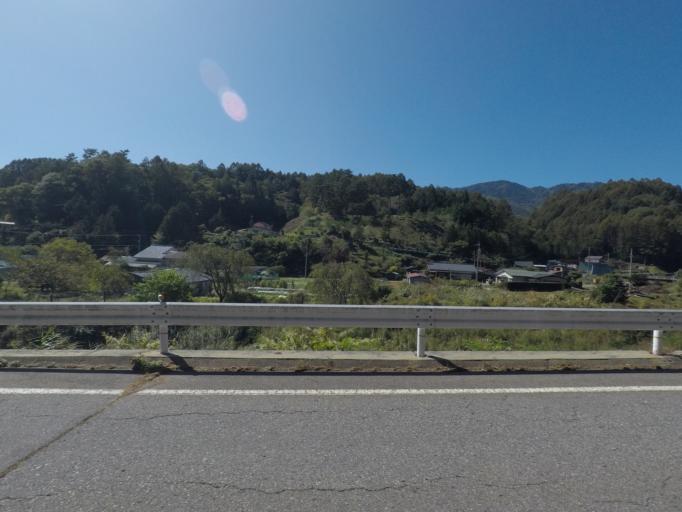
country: JP
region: Nagano
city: Shiojiri
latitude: 35.9815
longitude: 137.7459
